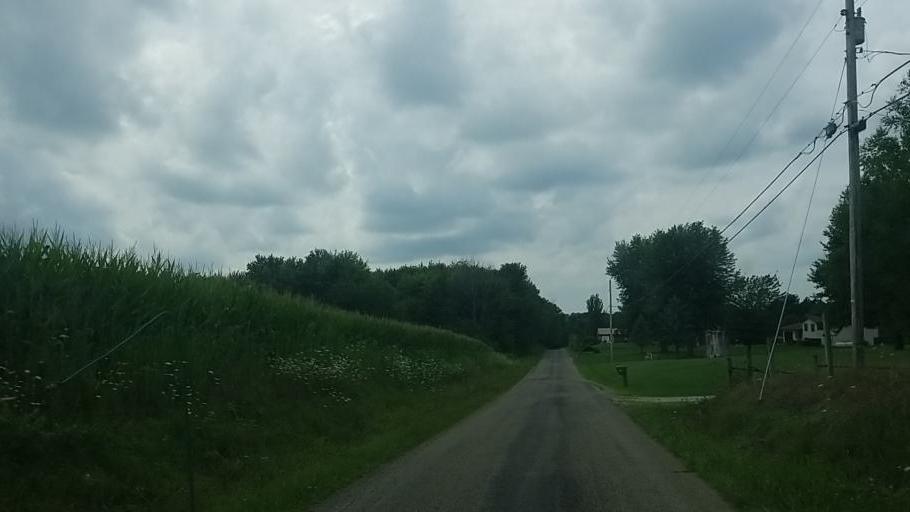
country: US
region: Ohio
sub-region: Knox County
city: Gambier
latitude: 40.2692
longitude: -82.3277
